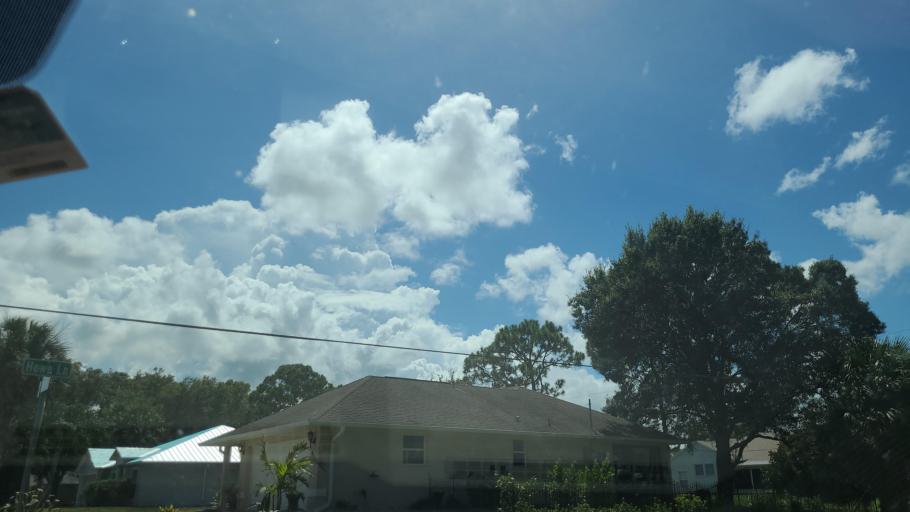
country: US
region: Florida
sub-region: Indian River County
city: Sebastian
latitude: 27.7745
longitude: -80.4903
